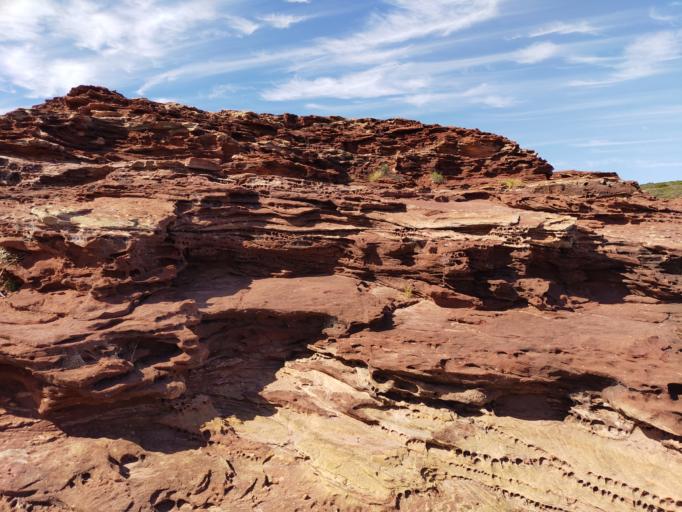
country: AU
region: Western Australia
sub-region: Northampton Shire
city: Kalbarri
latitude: -27.7444
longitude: 114.1430
